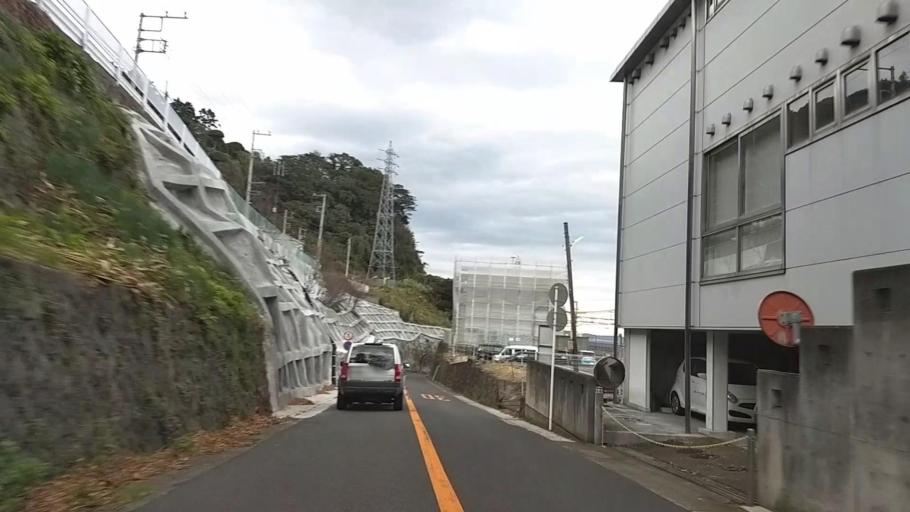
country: JP
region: Kanagawa
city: Odawara
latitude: 35.2035
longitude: 139.1388
